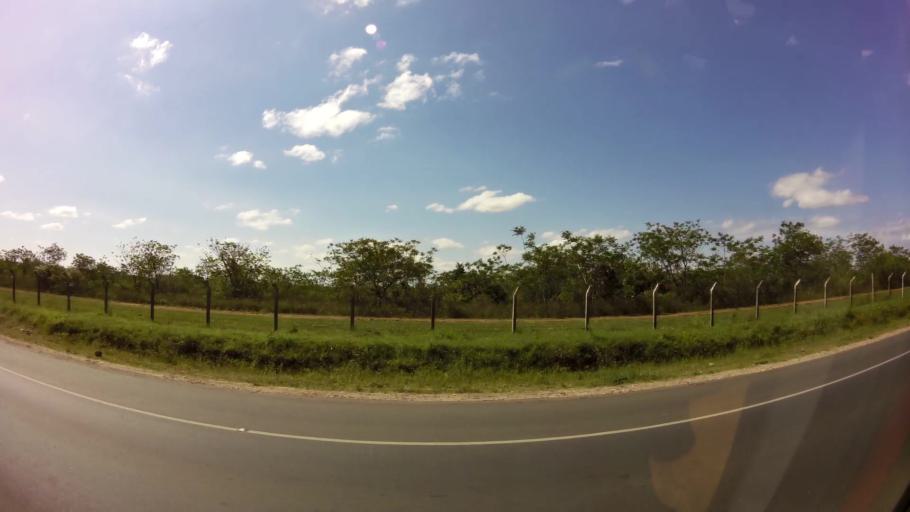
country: PY
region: Central
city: Fernando de la Mora
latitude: -25.2806
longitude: -57.5342
